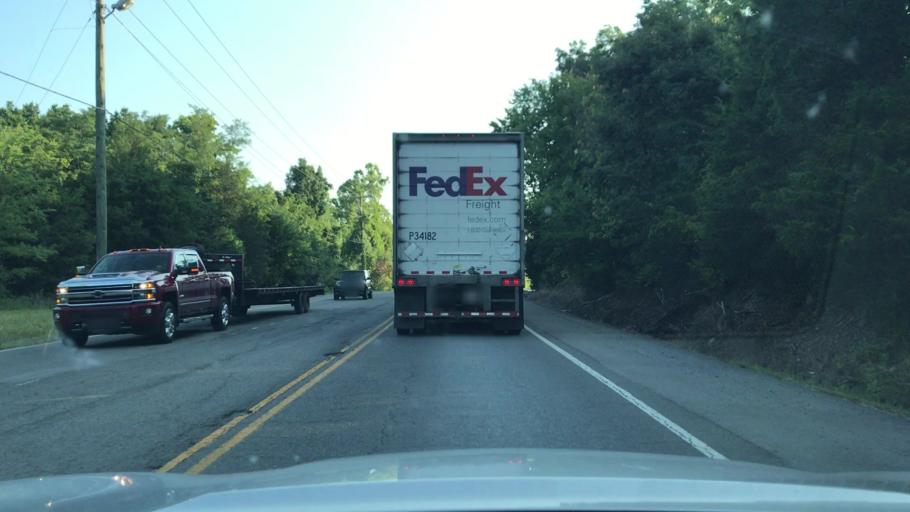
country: US
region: Tennessee
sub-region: Rutherford County
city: La Vergne
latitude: 36.0392
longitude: -86.6104
